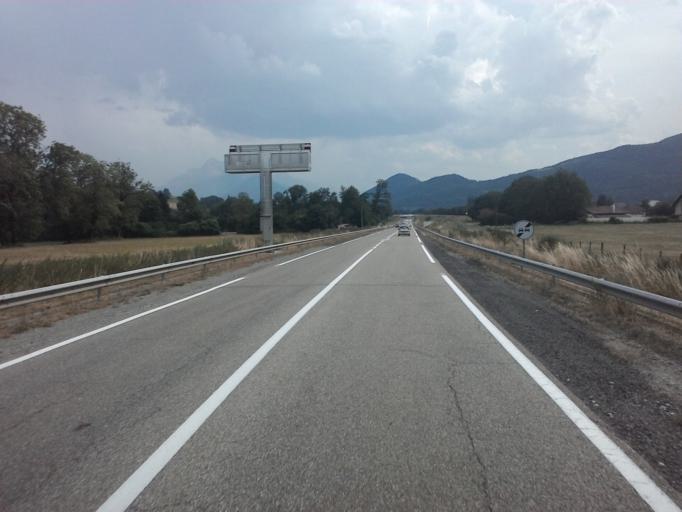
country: FR
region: Rhone-Alpes
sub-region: Departement de l'Isere
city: Pierre-Chatel
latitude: 44.9562
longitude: 5.7812
